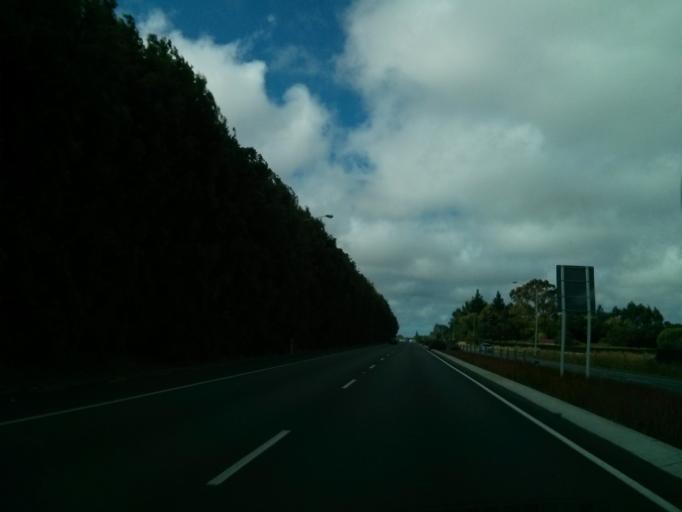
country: NZ
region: Canterbury
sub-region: Selwyn District
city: Prebbleton
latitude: -43.5077
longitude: 172.5413
